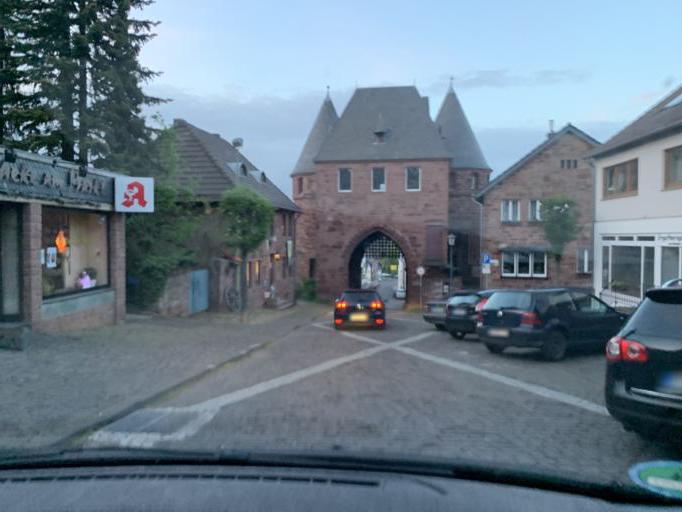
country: DE
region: North Rhine-Westphalia
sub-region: Regierungsbezirk Koln
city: Nideggen
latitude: 50.6901
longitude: 6.4822
